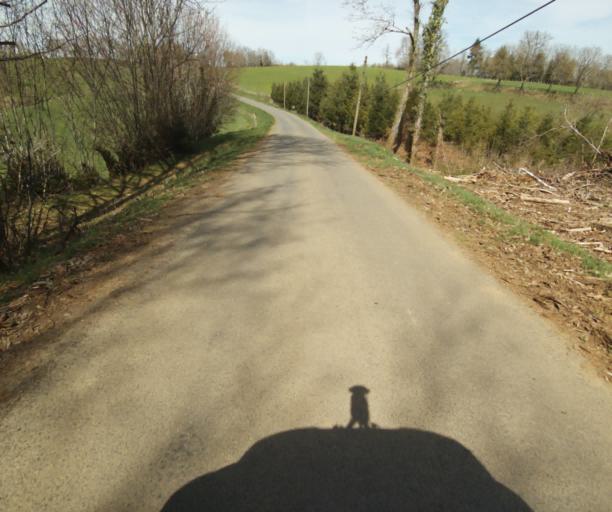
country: FR
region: Limousin
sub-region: Departement de la Correze
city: Naves
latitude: 45.3648
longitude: 1.7782
